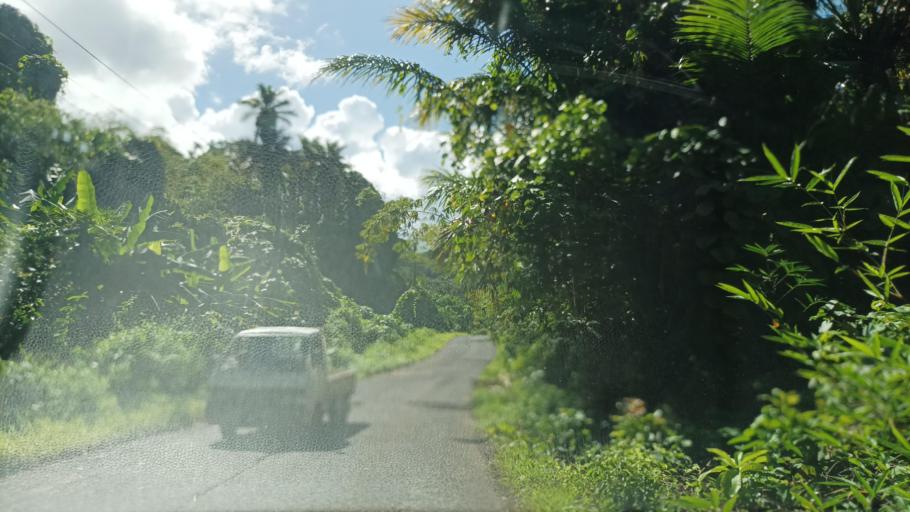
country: FM
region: Pohnpei
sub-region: Madolenihm Municipality
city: Madolenihm Municipality Government
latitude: 6.8490
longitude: 158.3001
